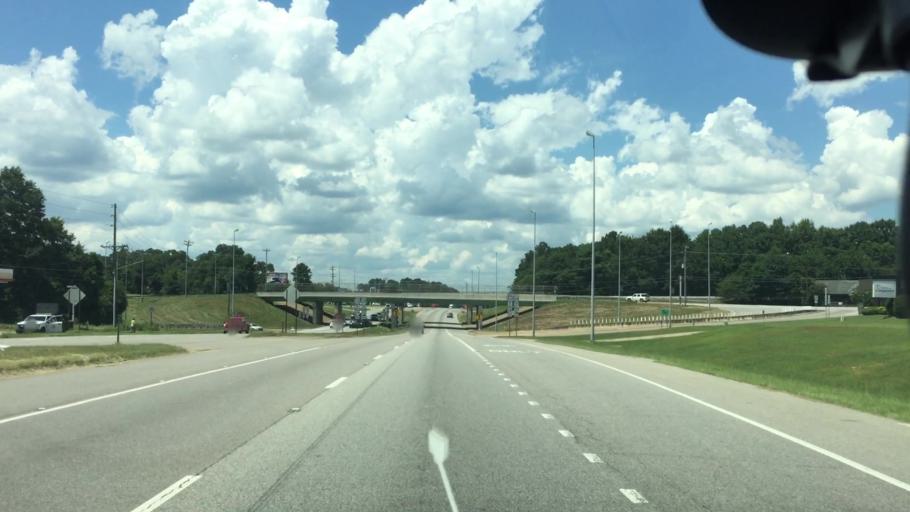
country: US
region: Alabama
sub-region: Pike County
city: Troy
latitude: 31.8044
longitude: -85.9870
